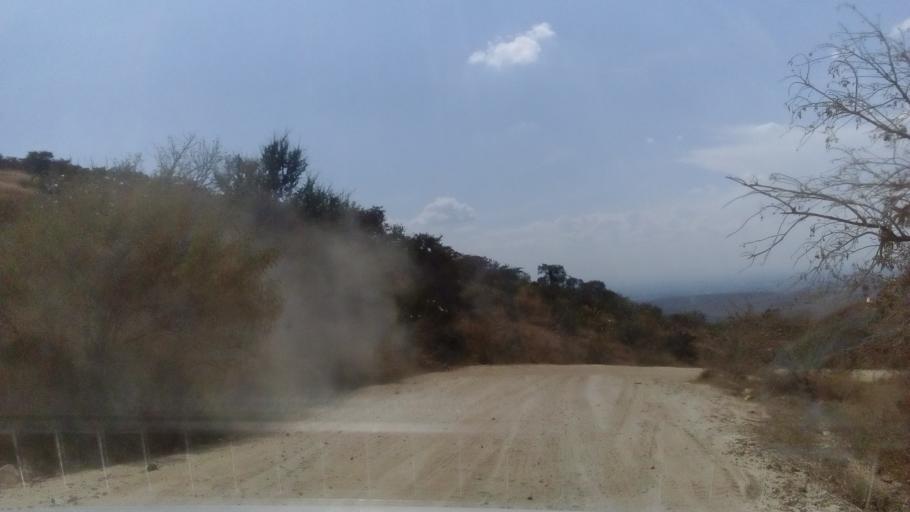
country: MX
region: Guanajuato
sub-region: Silao de la Victoria
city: Loma de Yerbabuena
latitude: 21.0807
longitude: -101.4496
